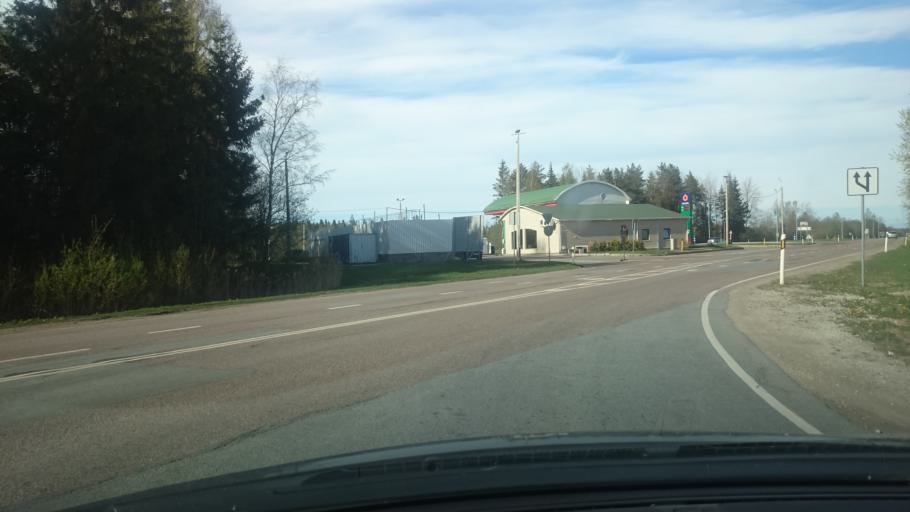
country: EE
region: Ida-Virumaa
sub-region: Johvi vald
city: Johvi
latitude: 59.3619
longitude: 27.4613
